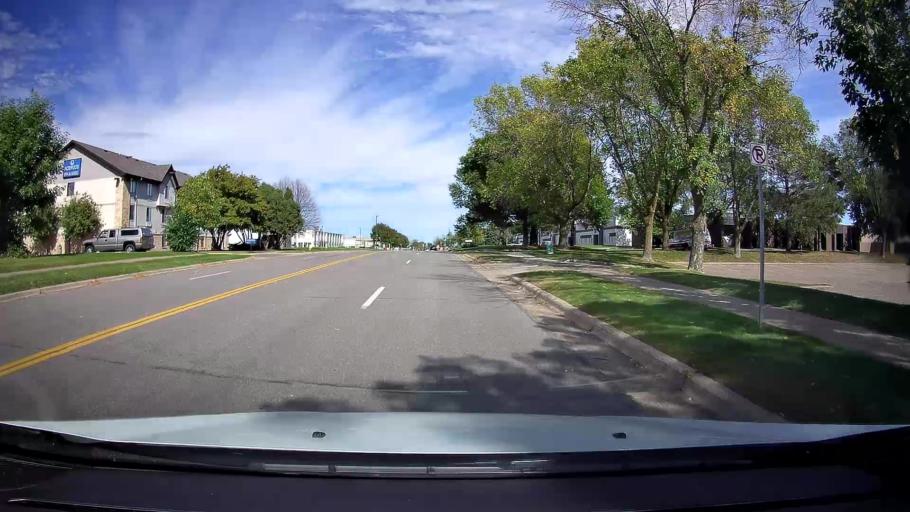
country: US
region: Minnesota
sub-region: Ramsey County
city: Falcon Heights
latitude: 45.0124
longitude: -93.1821
